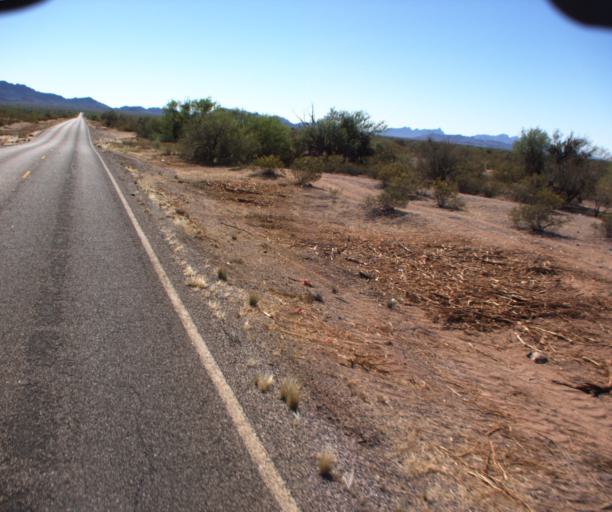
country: US
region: Arizona
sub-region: Pima County
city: Ajo
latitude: 32.3368
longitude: -112.7945
